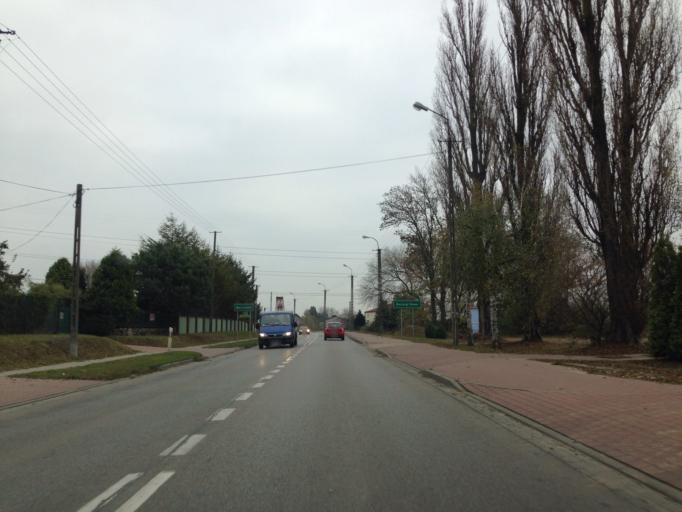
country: PL
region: Masovian Voivodeship
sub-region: Powiat warszawski zachodni
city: Hornowek
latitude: 52.2558
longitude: 20.7782
